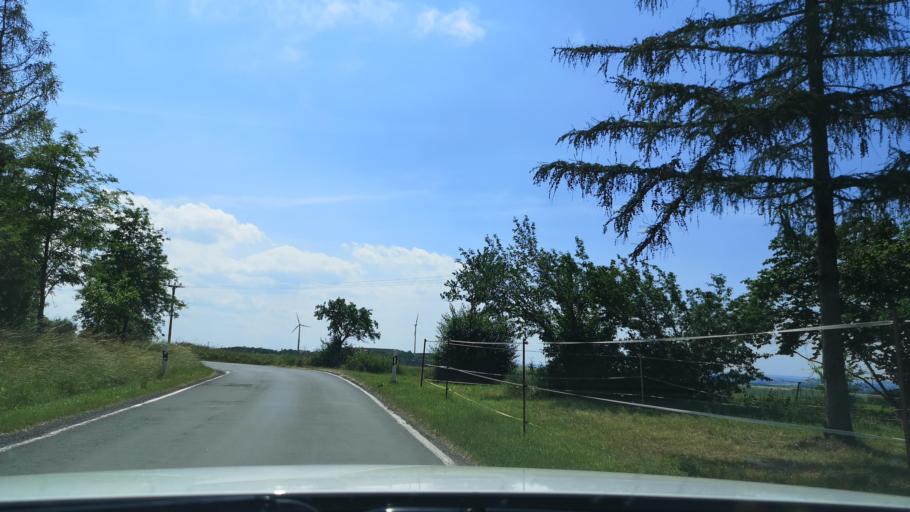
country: DE
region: Thuringia
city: Eberstedt
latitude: 51.0429
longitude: 11.5959
